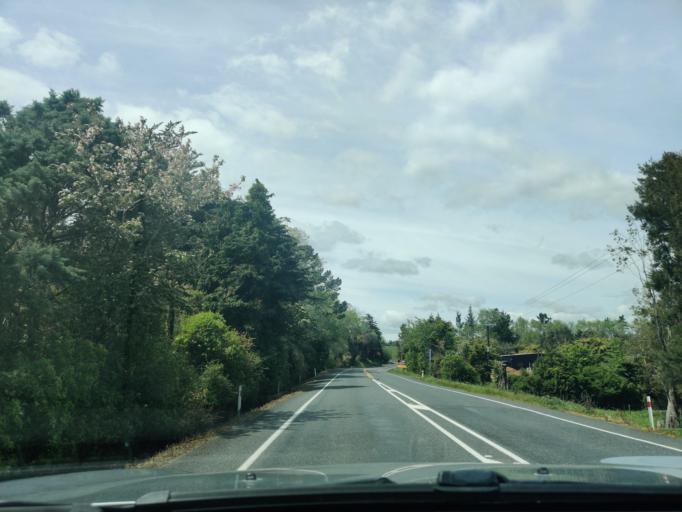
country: NZ
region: Taranaki
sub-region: New Plymouth District
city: New Plymouth
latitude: -39.1470
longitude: 174.1476
